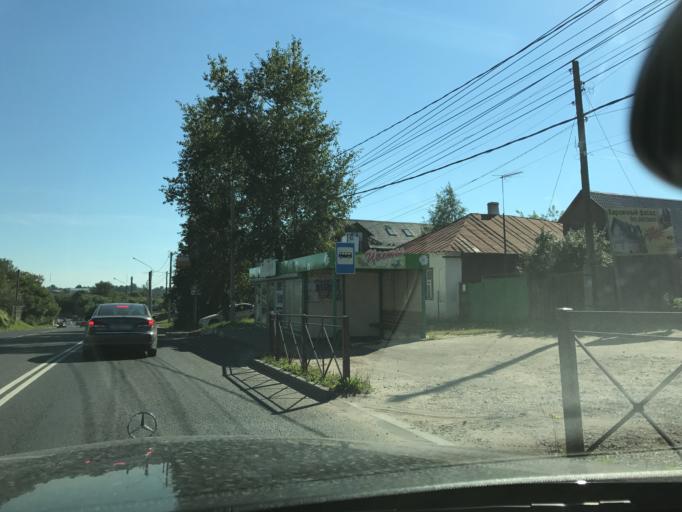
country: RU
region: Vladimir
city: Kirzhach
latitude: 56.1543
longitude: 38.8569
